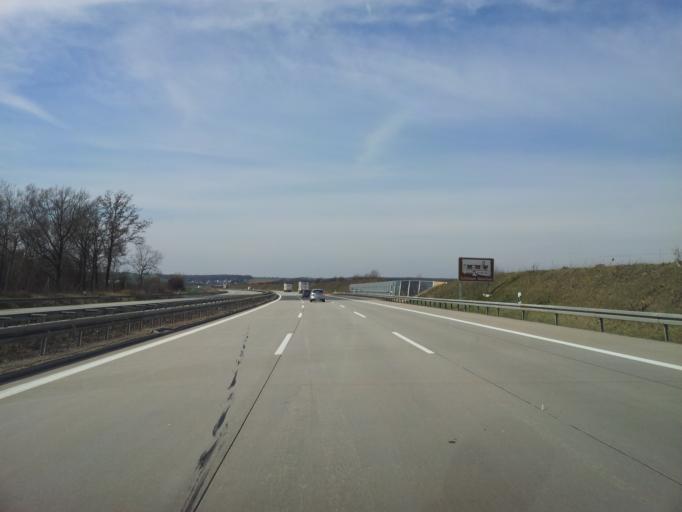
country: DE
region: Saxony
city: Remse
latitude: 50.8428
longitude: 12.5818
